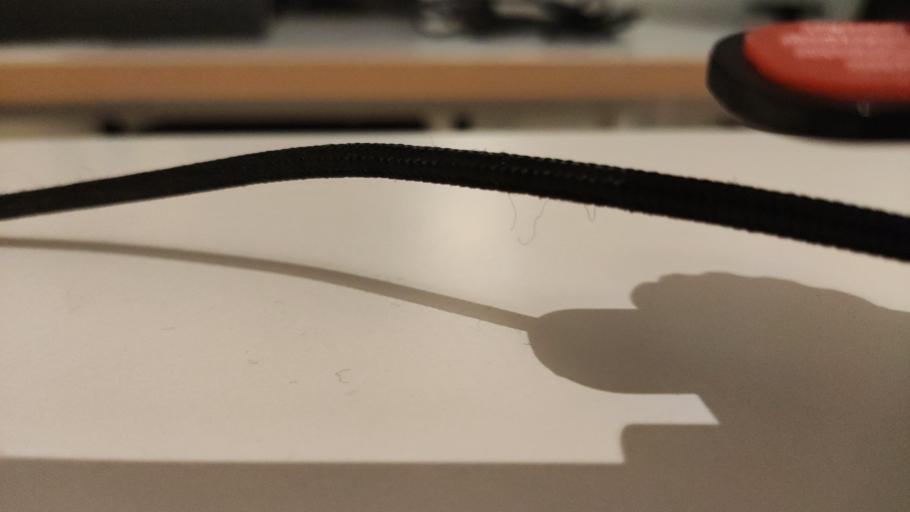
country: RU
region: Moskovskaya
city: Shaburnovo
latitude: 56.4248
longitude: 37.9629
